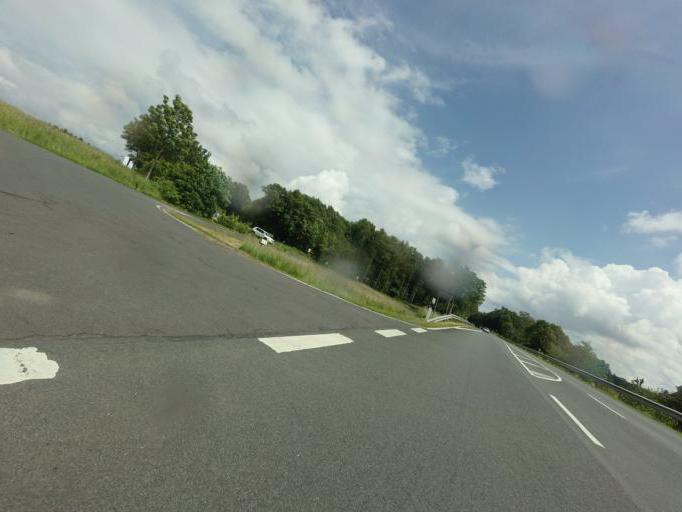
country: DE
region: Rheinland-Pfalz
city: Wirft
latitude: 50.3553
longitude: 6.8733
